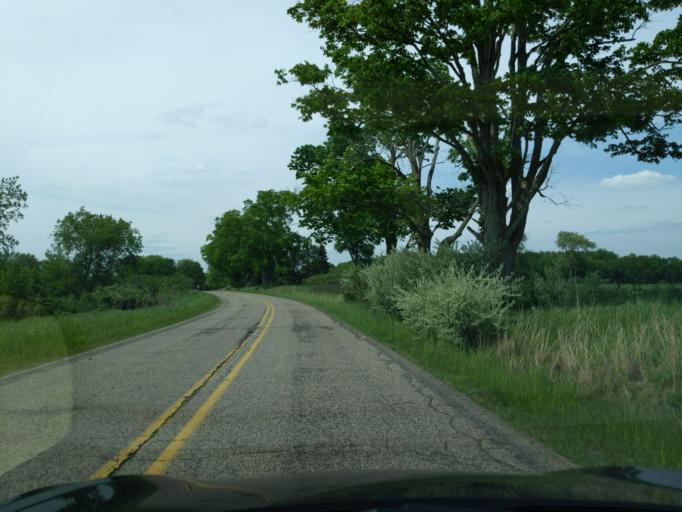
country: US
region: Michigan
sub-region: Ingham County
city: Leslie
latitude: 42.4231
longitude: -84.3336
